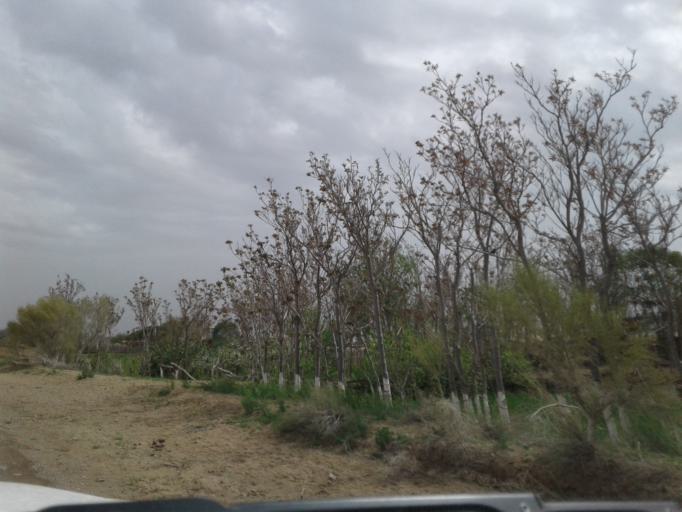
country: TM
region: Lebap
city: Atamyrat
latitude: 38.1702
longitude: 64.9138
